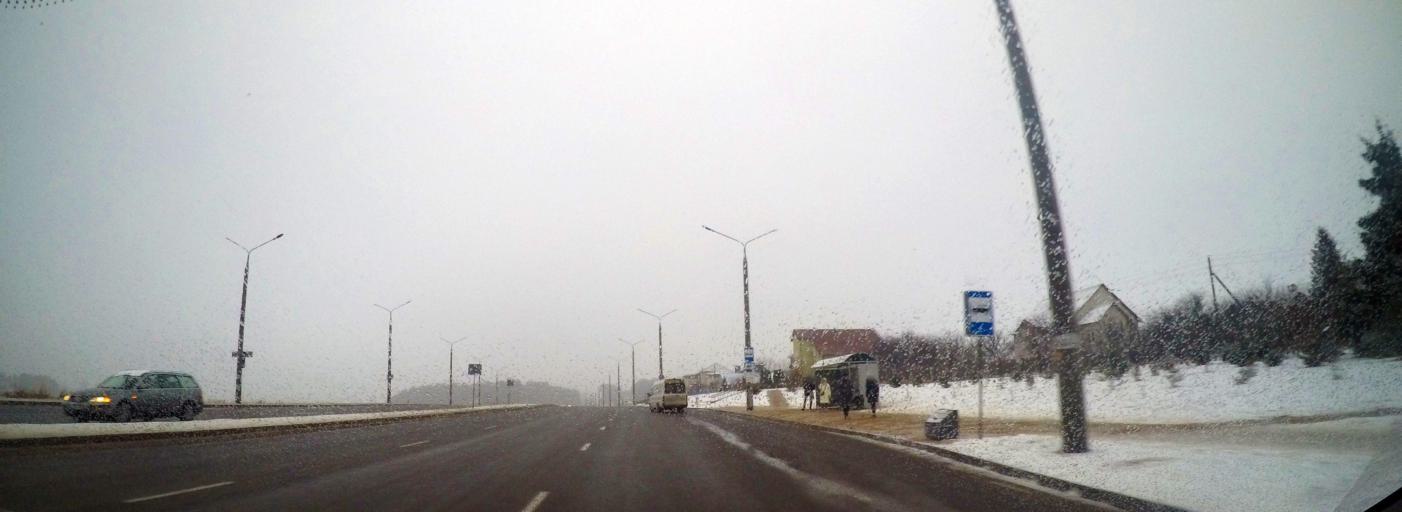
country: BY
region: Grodnenskaya
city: Hrodna
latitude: 53.6273
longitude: 23.8035
